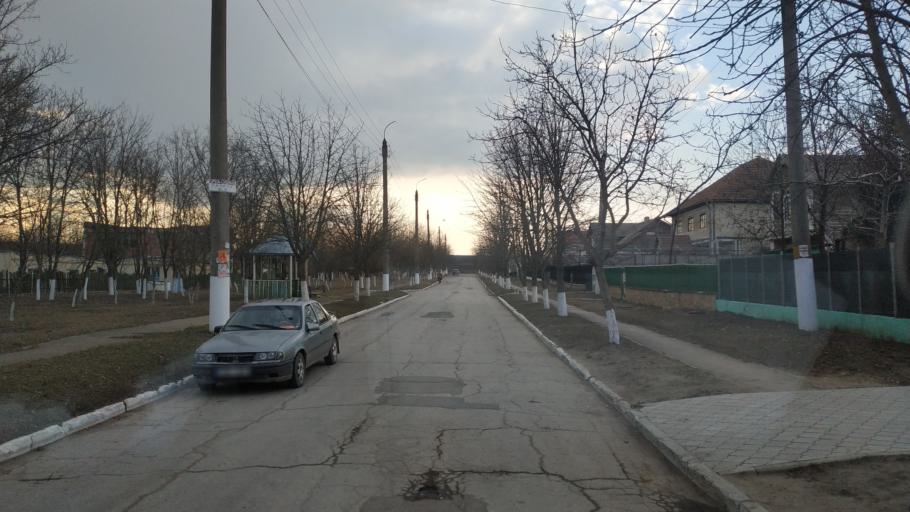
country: MD
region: Telenesti
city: Grigoriopol
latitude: 47.0124
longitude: 29.2916
